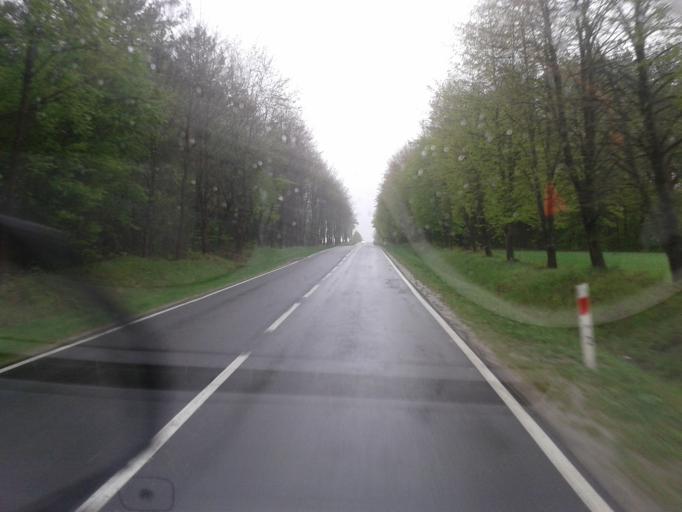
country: PL
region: Subcarpathian Voivodeship
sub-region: Powiat lubaczowski
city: Narol
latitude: 50.3268
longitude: 23.2804
